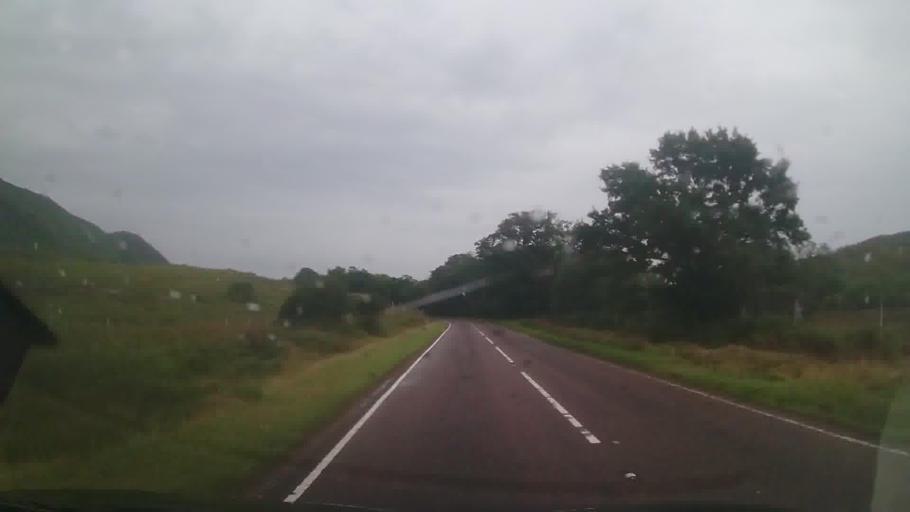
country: GB
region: Scotland
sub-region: Argyll and Bute
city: Oban
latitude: 56.6802
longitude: -5.3718
